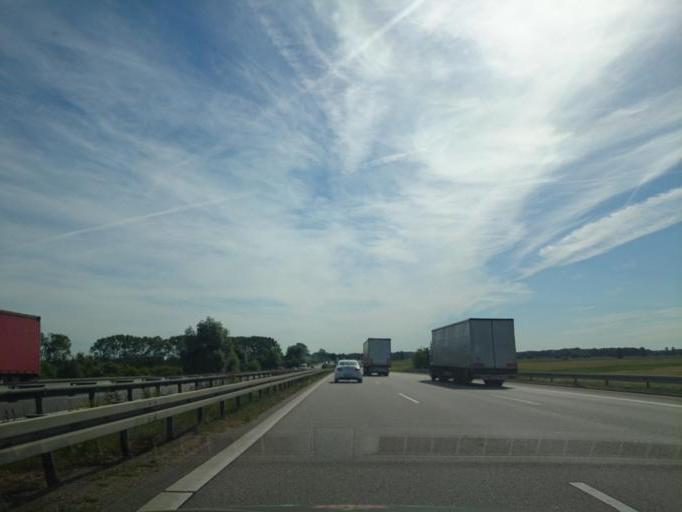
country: DE
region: Brandenburg
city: Grossbeeren
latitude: 52.3067
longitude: 13.3393
